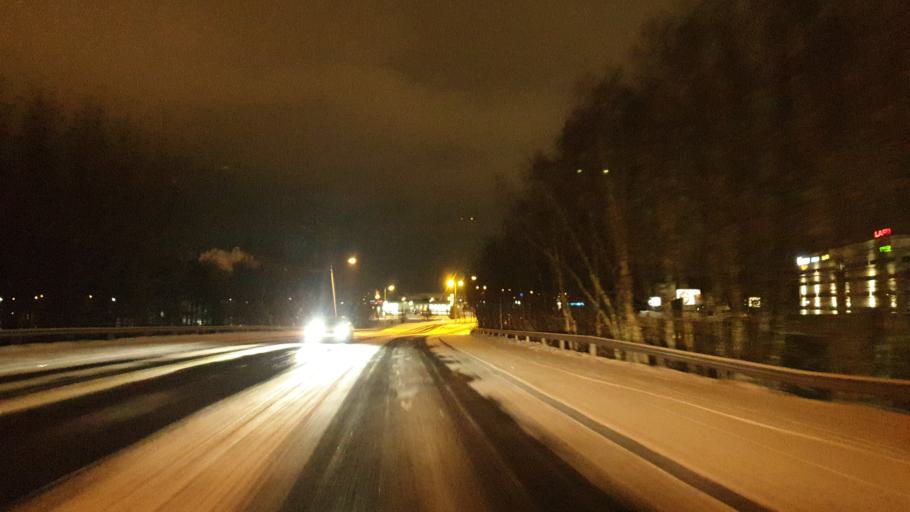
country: FI
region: Northern Ostrobothnia
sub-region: Oulu
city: Oulu
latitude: 64.9894
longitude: 25.4684
